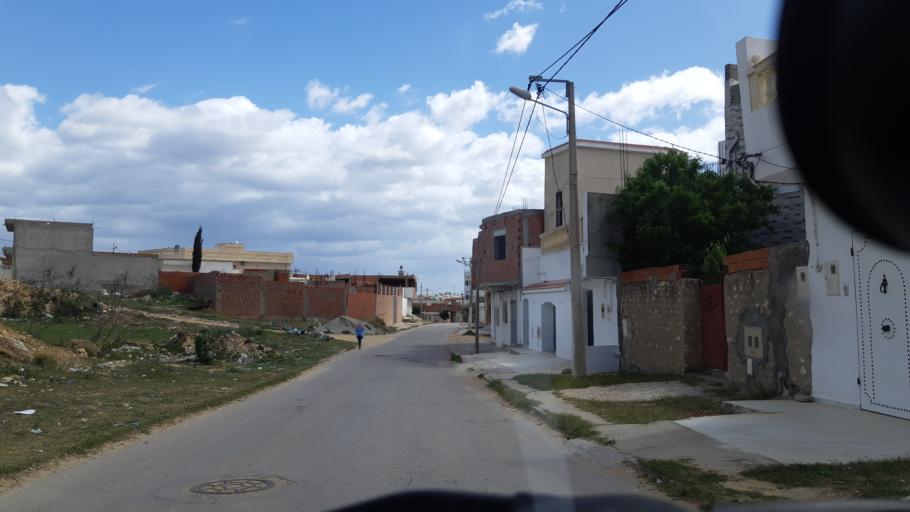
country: TN
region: Susah
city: Akouda
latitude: 35.8767
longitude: 10.5178
